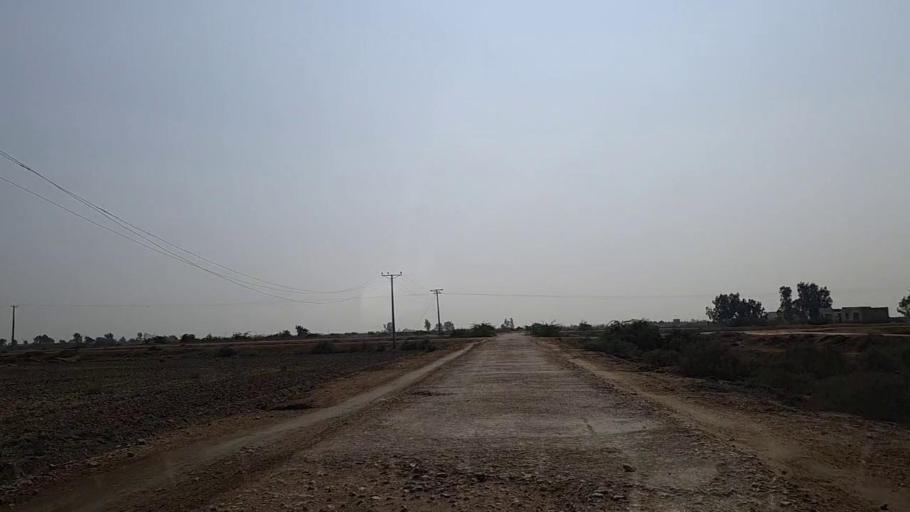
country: PK
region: Sindh
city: Thatta
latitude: 24.7123
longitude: 67.7685
